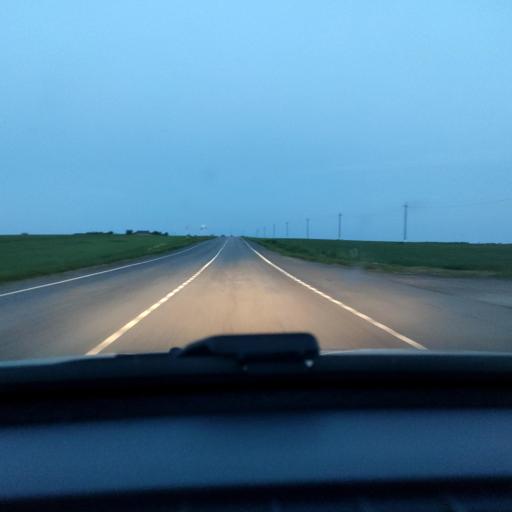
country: RU
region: Voronezj
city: Verkhnyaya Khava
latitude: 51.6881
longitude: 39.9319
